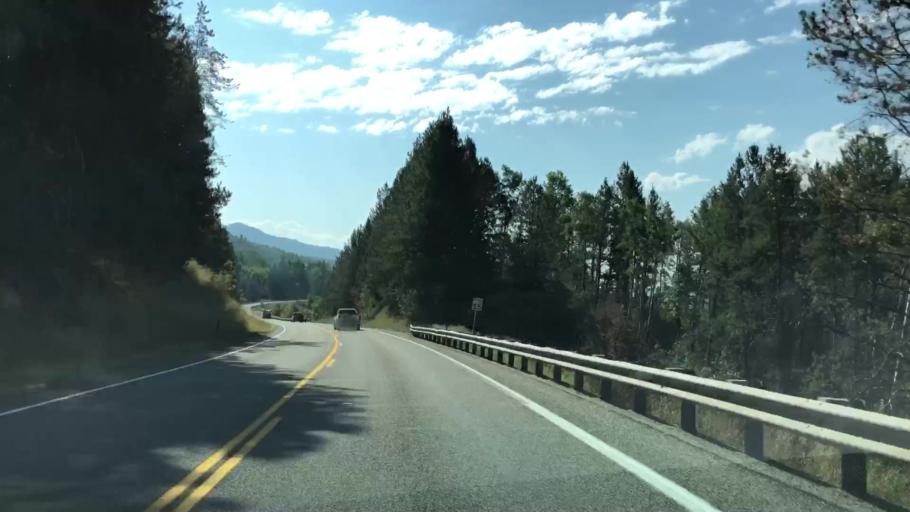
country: US
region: Idaho
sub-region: Teton County
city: Victor
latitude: 43.3039
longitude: -111.1340
